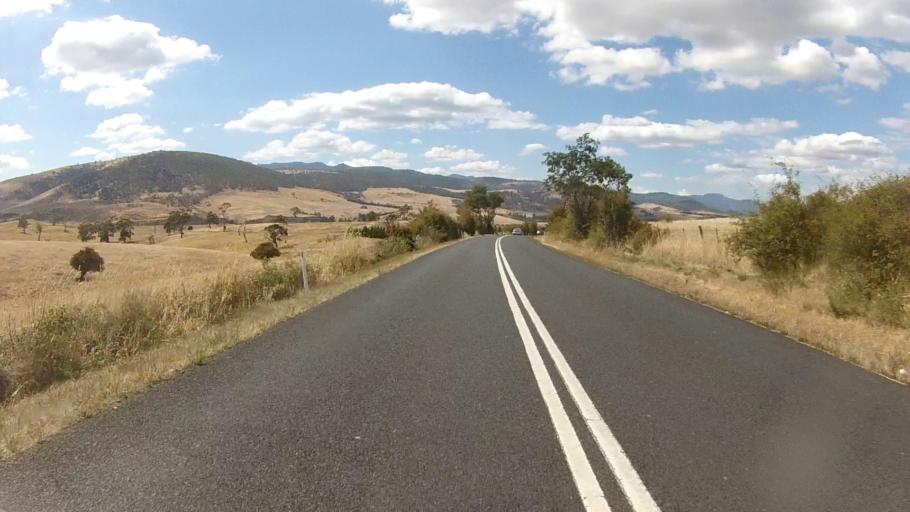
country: AU
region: Tasmania
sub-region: Derwent Valley
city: New Norfolk
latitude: -42.7359
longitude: 146.9389
